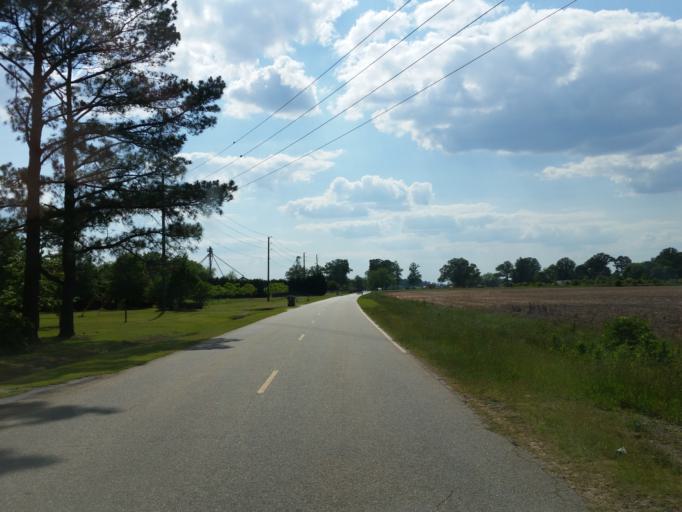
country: US
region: Georgia
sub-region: Houston County
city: Centerville
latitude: 32.5783
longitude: -83.7229
